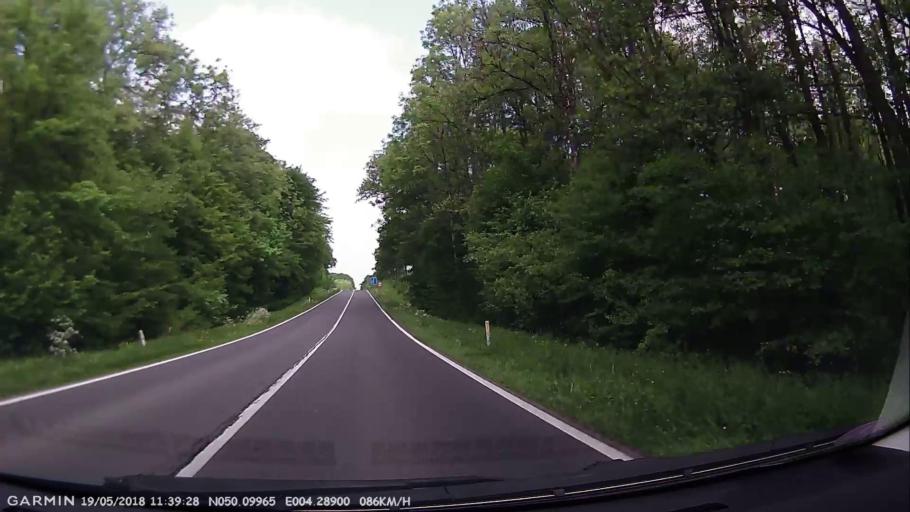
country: BE
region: Wallonia
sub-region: Province du Hainaut
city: Chimay
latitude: 50.1000
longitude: 4.2889
